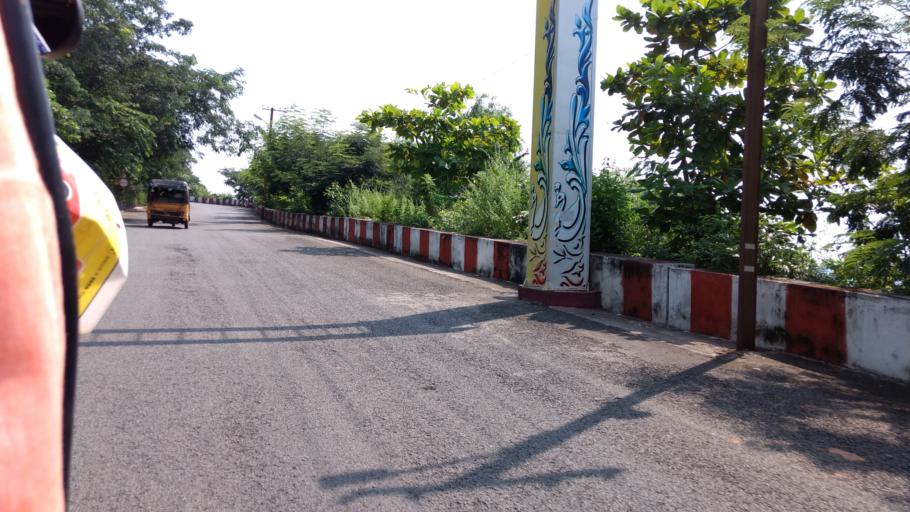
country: IN
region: Andhra Pradesh
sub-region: East Godavari
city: Tuni
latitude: 17.2806
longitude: 82.3988
